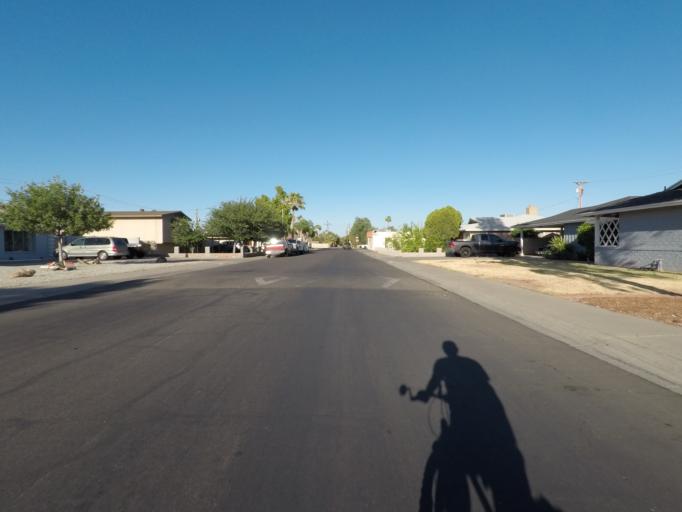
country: US
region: Arizona
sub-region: Maricopa County
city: Phoenix
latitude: 33.5041
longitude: -112.1013
